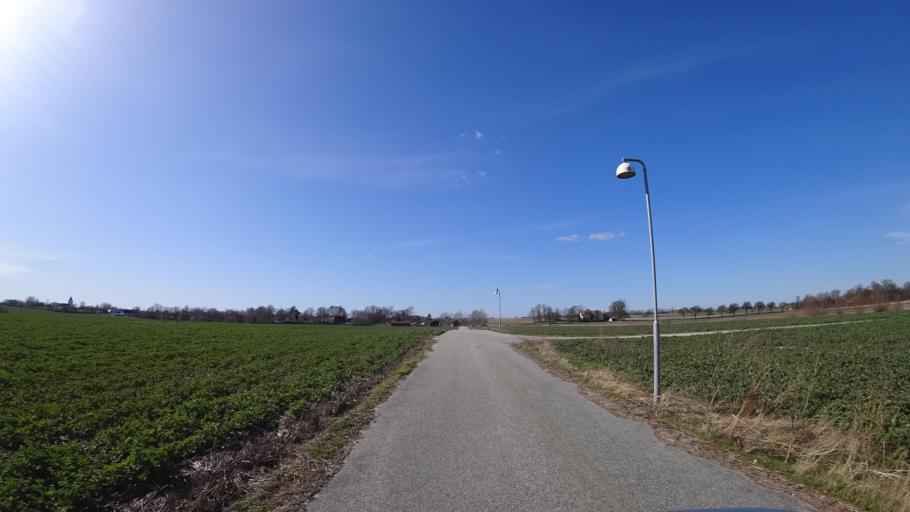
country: SE
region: Skane
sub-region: Staffanstorps Kommun
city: Staffanstorp
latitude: 55.6269
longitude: 13.1721
